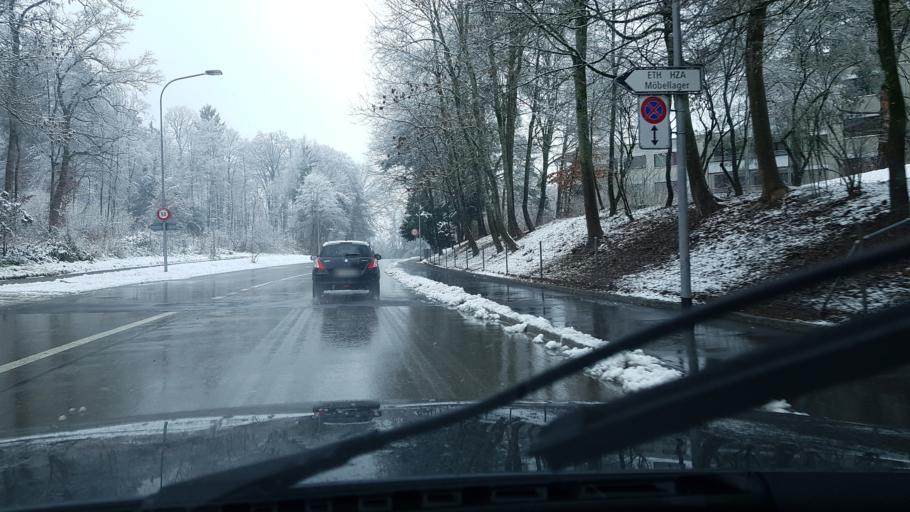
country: CH
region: Zurich
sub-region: Bezirk Zuerich
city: Zuerich (Kreis 10)
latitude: 47.4124
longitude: 8.5062
